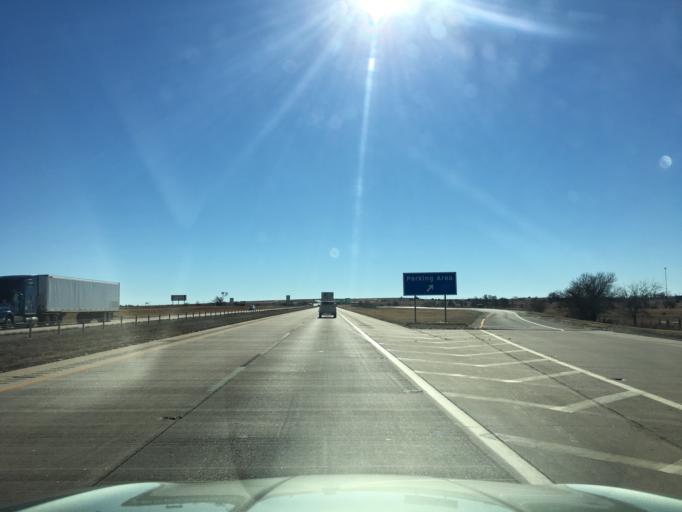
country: US
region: Oklahoma
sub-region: Noble County
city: Perry
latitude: 36.4155
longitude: -97.3272
